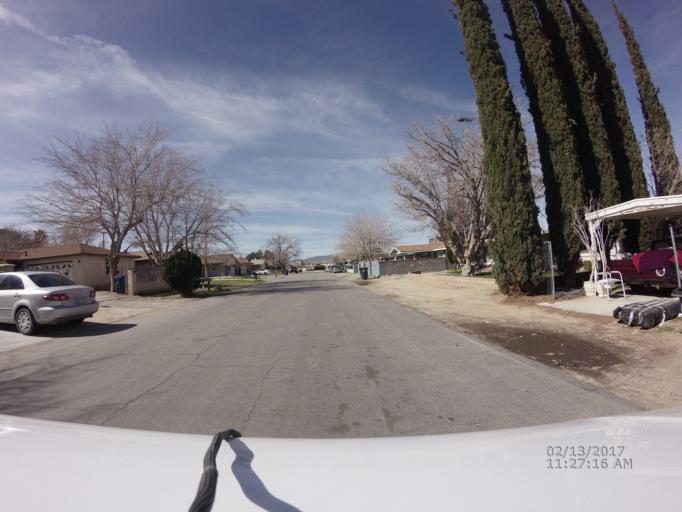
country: US
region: California
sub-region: Los Angeles County
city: Littlerock
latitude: 34.5260
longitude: -117.9983
